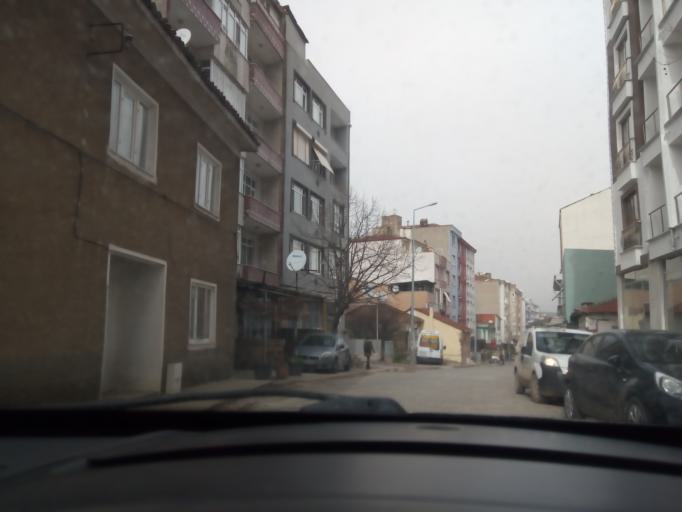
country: TR
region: Balikesir
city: Susurluk
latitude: 39.9106
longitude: 28.1581
